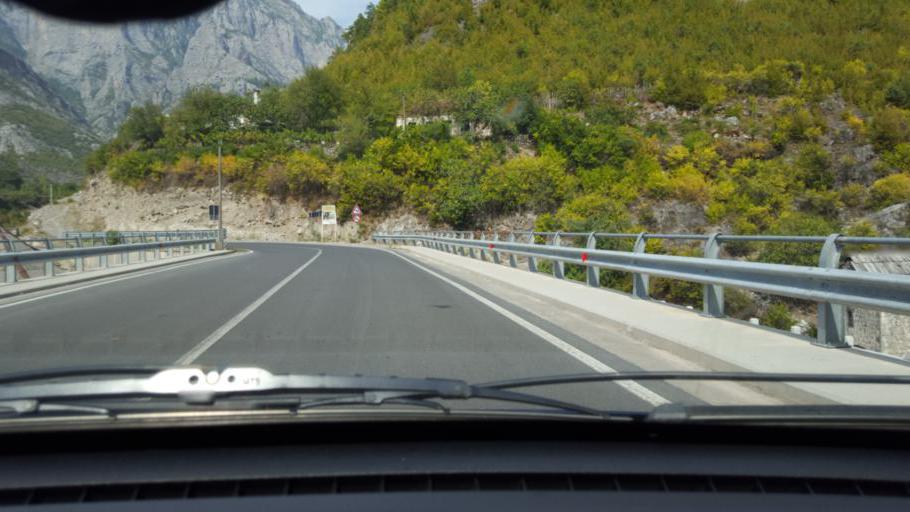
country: AL
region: Shkoder
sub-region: Rrethi i Malesia e Madhe
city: Kastrat
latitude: 42.4545
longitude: 19.5612
